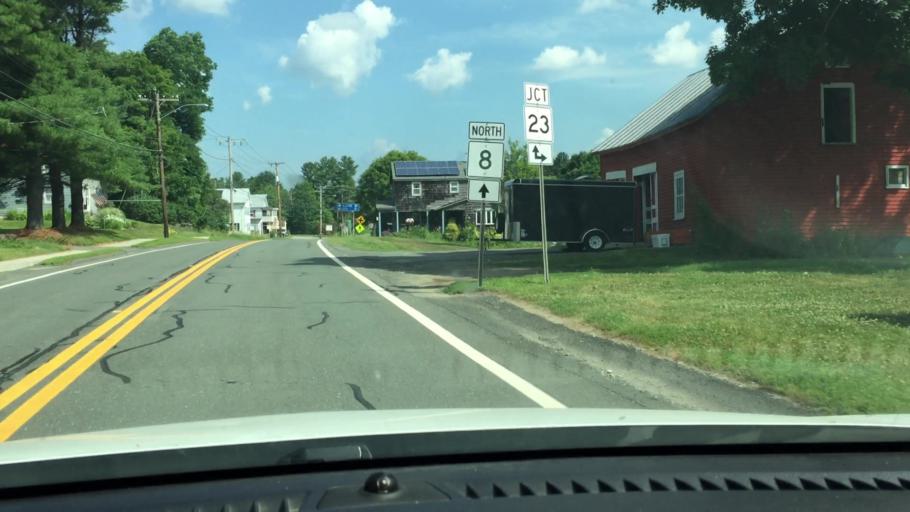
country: US
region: Massachusetts
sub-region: Berkshire County
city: Otis
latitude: 42.1911
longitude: -73.0914
